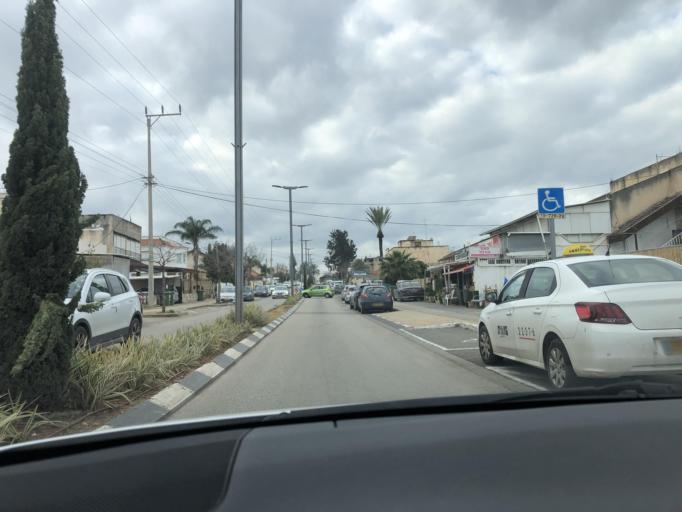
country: IL
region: Central District
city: Rosh Ha'Ayin
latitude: 32.0950
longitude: 34.9544
